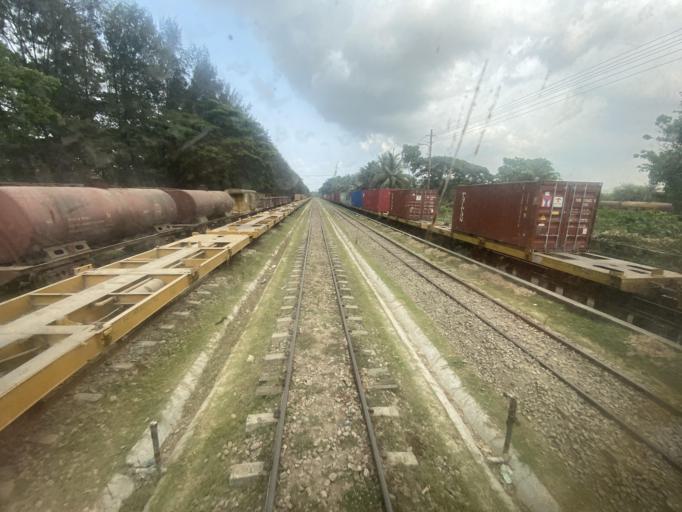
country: BD
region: Chittagong
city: Chittagong
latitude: 22.3213
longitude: 91.7827
